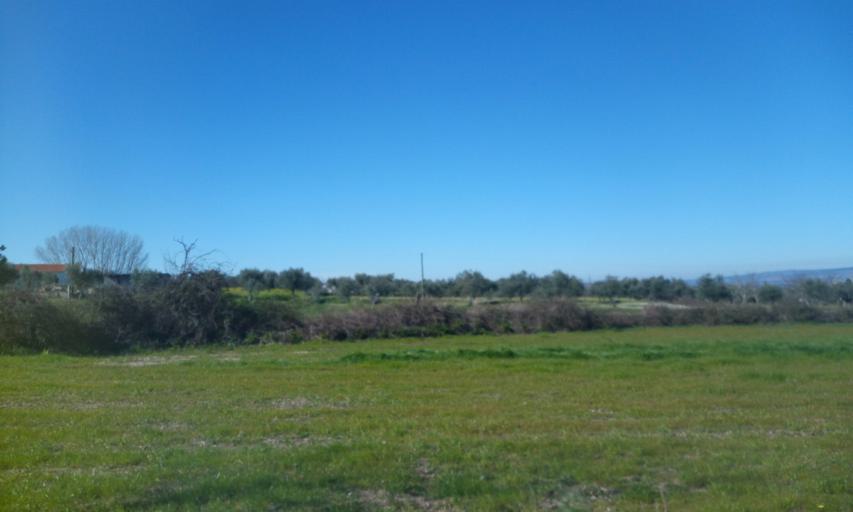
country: PT
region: Guarda
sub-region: Fornos de Algodres
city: Fornos de Algodres
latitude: 40.5279
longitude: -7.5571
